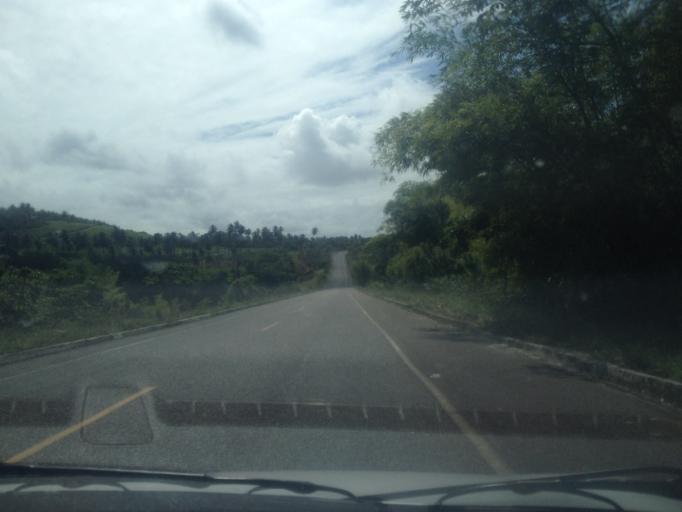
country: BR
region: Bahia
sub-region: Conde
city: Conde
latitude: -11.8968
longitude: -37.6520
